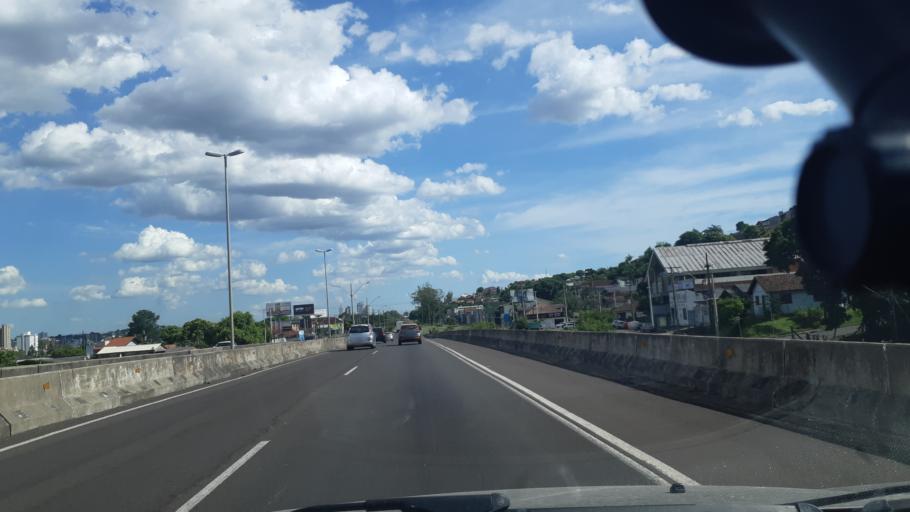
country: BR
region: Rio Grande do Sul
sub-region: Novo Hamburgo
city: Novo Hamburgo
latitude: -29.6705
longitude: -51.1431
